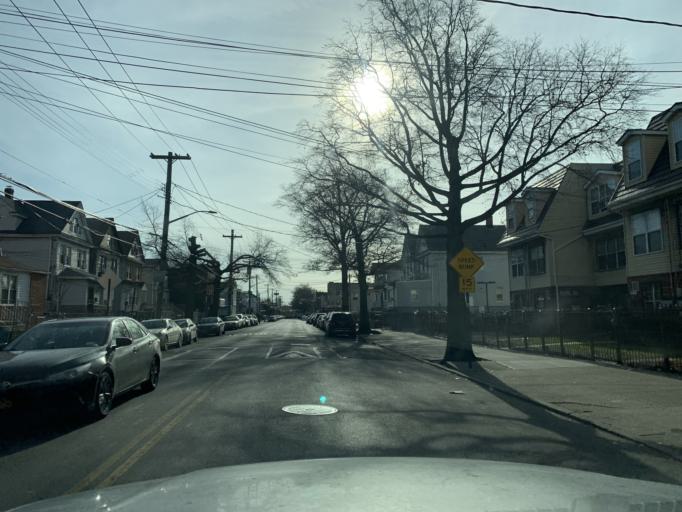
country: US
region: New York
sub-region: Queens County
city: Jamaica
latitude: 40.6977
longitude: -73.7921
